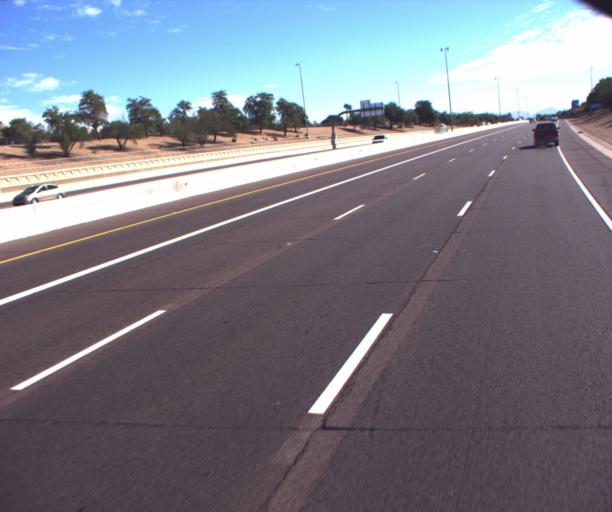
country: US
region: Arizona
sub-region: Maricopa County
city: Sun City
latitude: 33.6677
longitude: -112.2200
